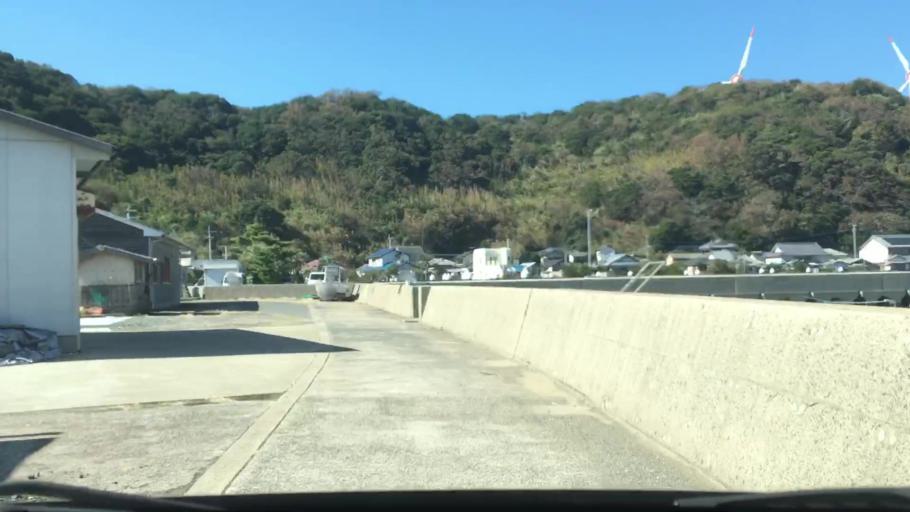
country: JP
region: Nagasaki
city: Sasebo
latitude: 33.0020
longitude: 129.5540
